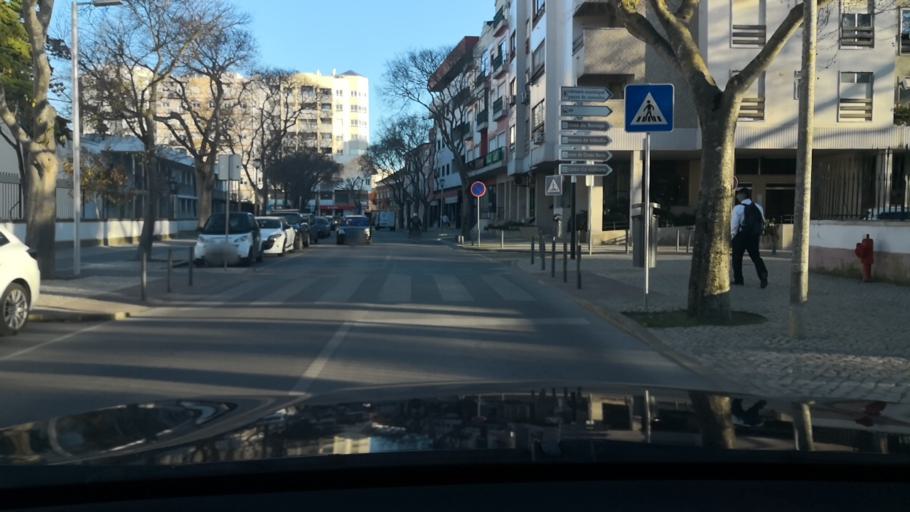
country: PT
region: Setubal
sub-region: Setubal
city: Setubal
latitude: 38.5265
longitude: -8.8924
